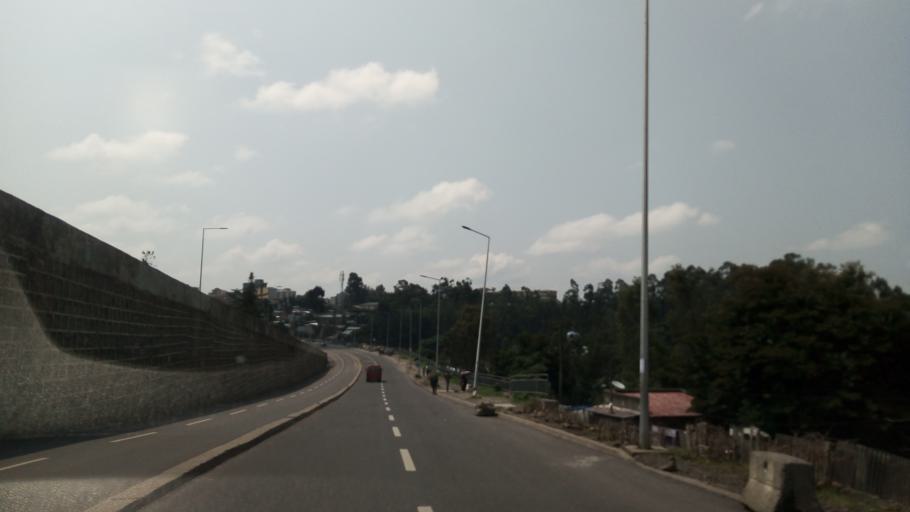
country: ET
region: Adis Abeba
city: Addis Ababa
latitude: 8.9829
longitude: 38.7670
